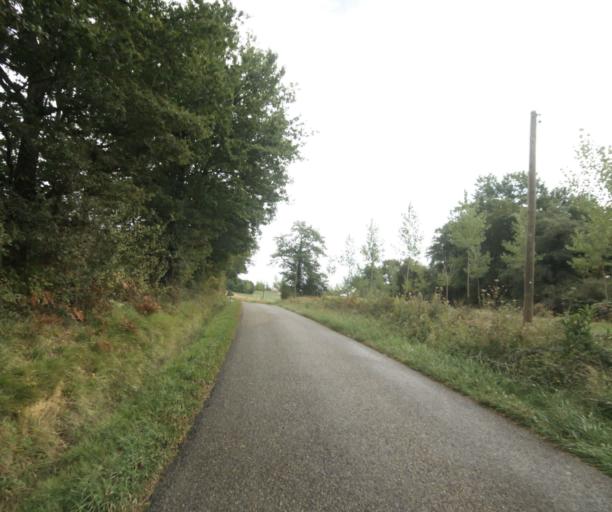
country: FR
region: Midi-Pyrenees
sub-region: Departement du Gers
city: Cazaubon
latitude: 43.8930
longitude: -0.1204
